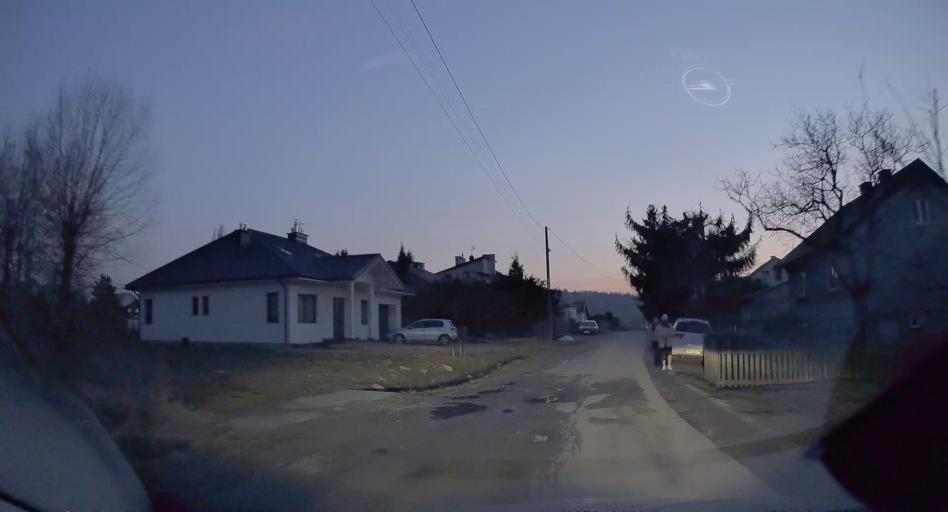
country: PL
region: Subcarpathian Voivodeship
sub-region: Powiat debicki
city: Debica
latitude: 50.0267
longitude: 21.3894
